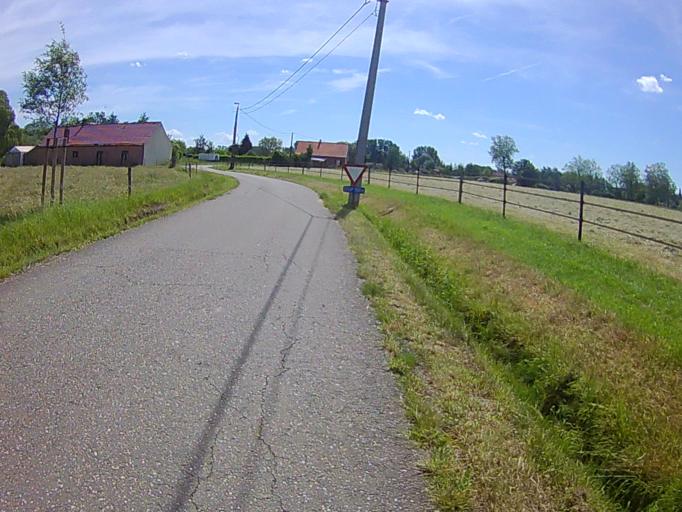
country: BE
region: Flanders
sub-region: Provincie Antwerpen
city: Nijlen
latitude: 51.1800
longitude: 4.6294
